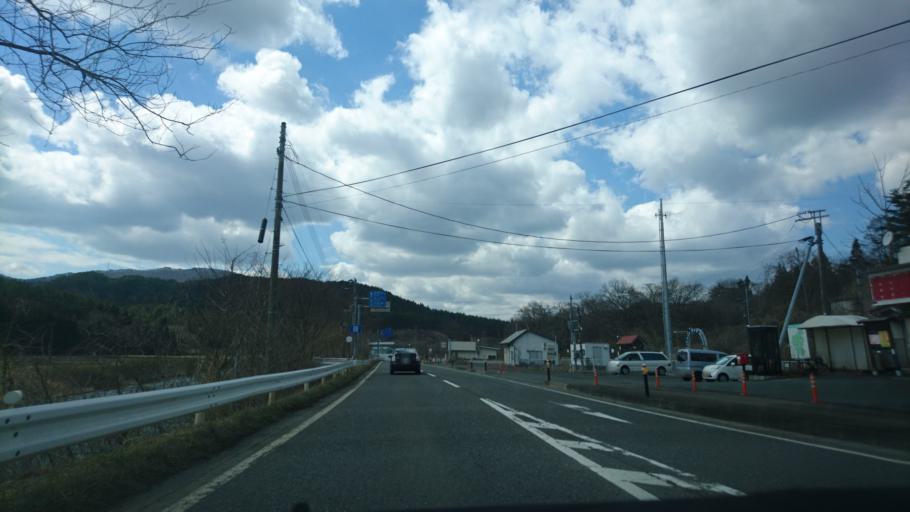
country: JP
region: Iwate
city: Tono
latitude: 39.3000
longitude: 141.4006
